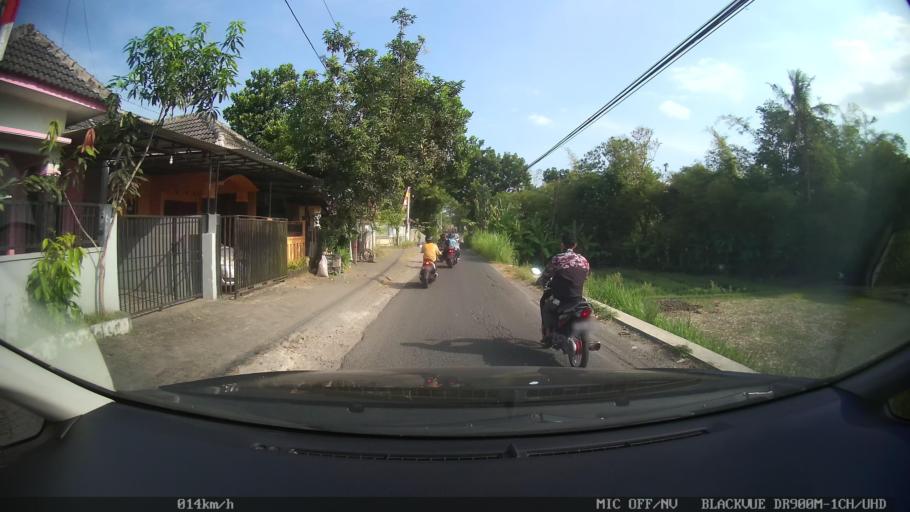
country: ID
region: Daerah Istimewa Yogyakarta
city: Kasihan
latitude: -7.8309
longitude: 110.3235
